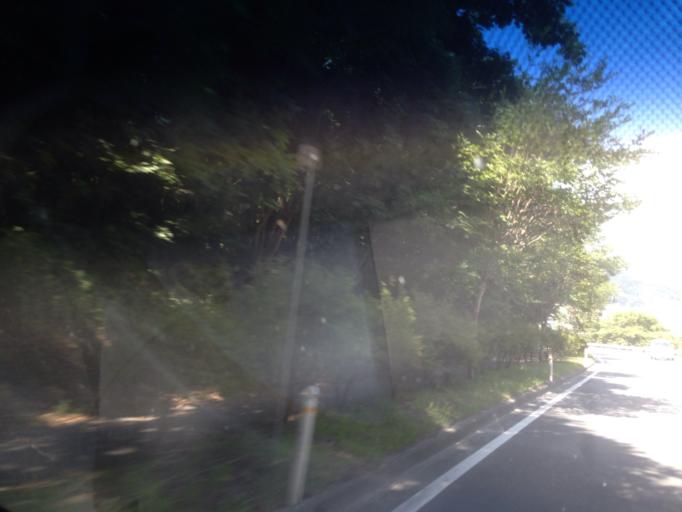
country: JP
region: Iwate
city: Kamaishi
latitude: 39.3182
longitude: 141.8835
